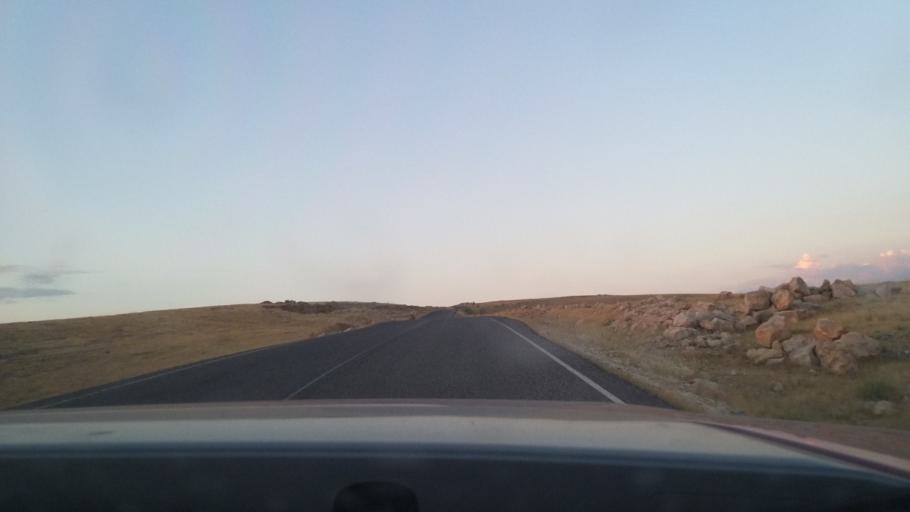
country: TR
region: Batman
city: Erkoklu
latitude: 37.7807
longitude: 41.1328
